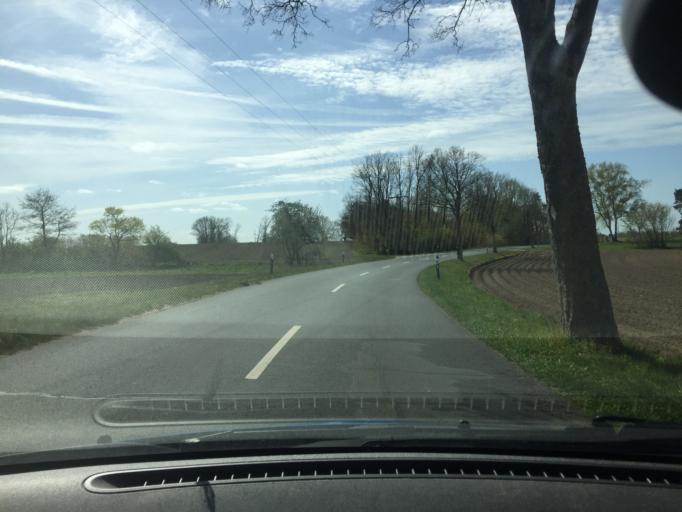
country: DE
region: Lower Saxony
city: Ratzlingen
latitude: 52.9707
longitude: 10.6789
